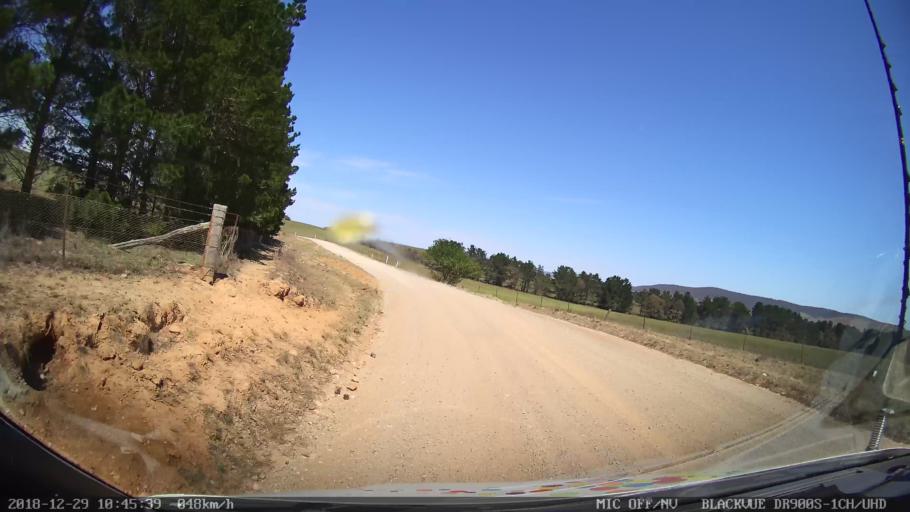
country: AU
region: New South Wales
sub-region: Palerang
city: Bungendore
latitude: -35.0449
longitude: 149.5190
